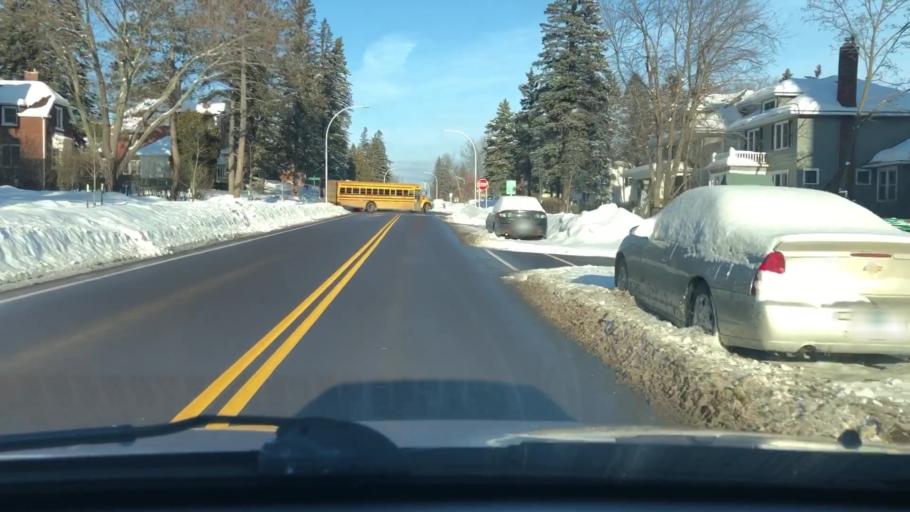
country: US
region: Minnesota
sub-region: Saint Louis County
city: Duluth
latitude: 46.8120
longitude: -92.0734
